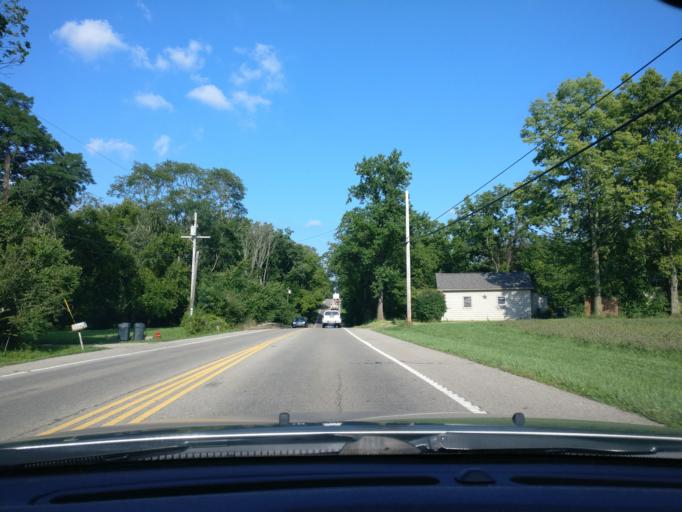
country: US
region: Ohio
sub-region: Warren County
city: Five Points
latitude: 39.5463
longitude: -84.1521
